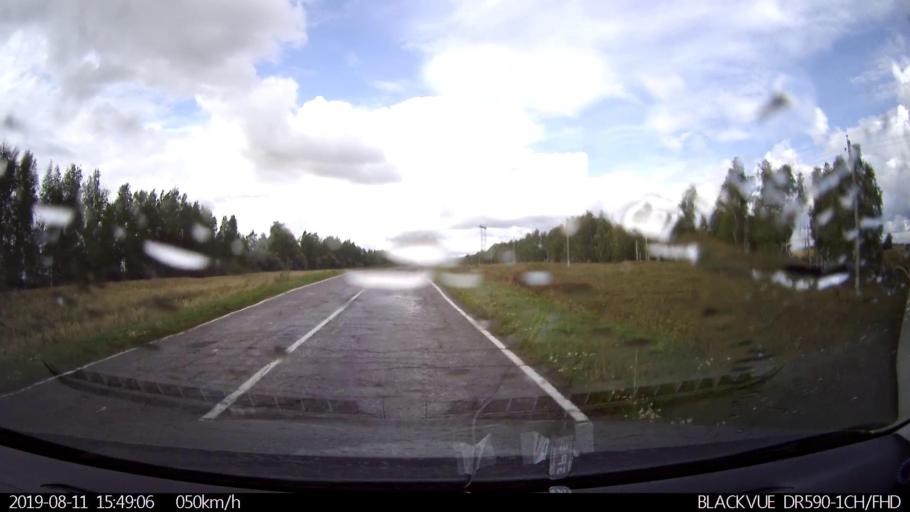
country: RU
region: Ulyanovsk
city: Ignatovka
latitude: 53.9018
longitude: 47.6547
